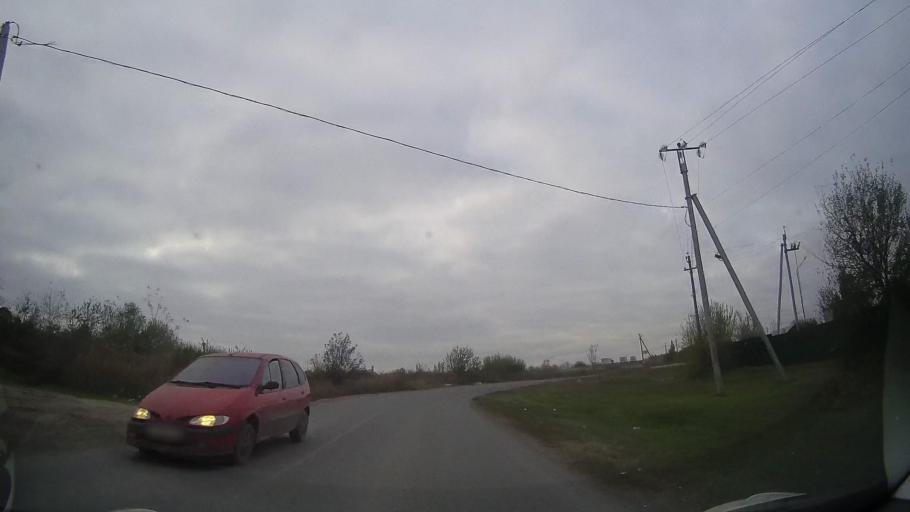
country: RU
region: Rostov
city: Bataysk
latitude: 47.0888
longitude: 39.7655
